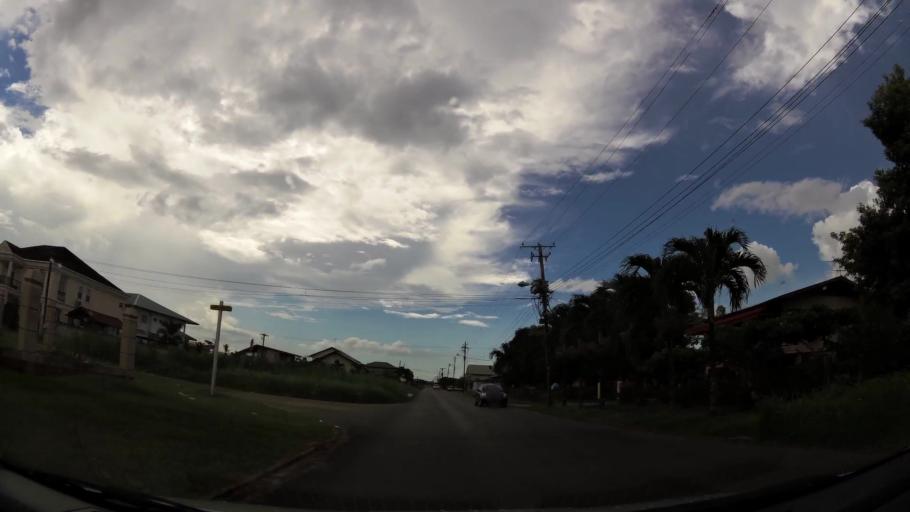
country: SR
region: Paramaribo
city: Paramaribo
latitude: 5.8453
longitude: -55.1286
